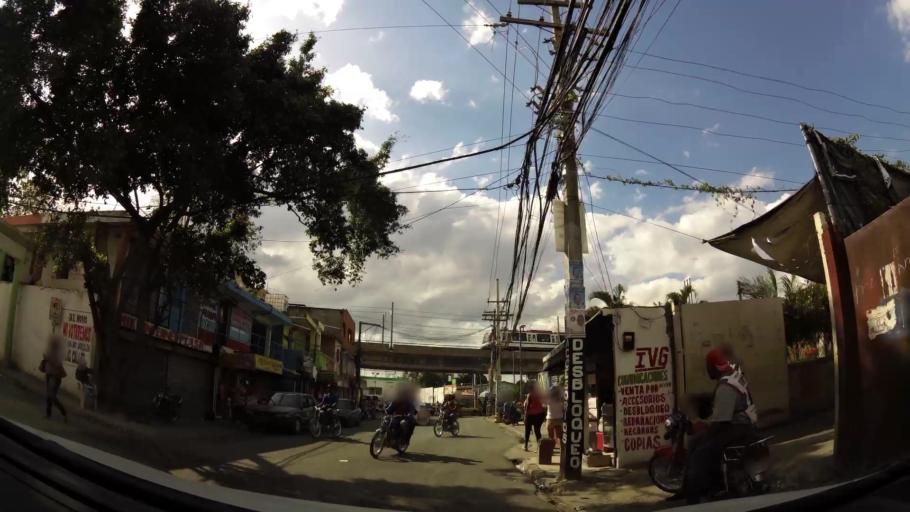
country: DO
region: Nacional
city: Ensanche Luperon
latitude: 18.5443
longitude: -69.8998
